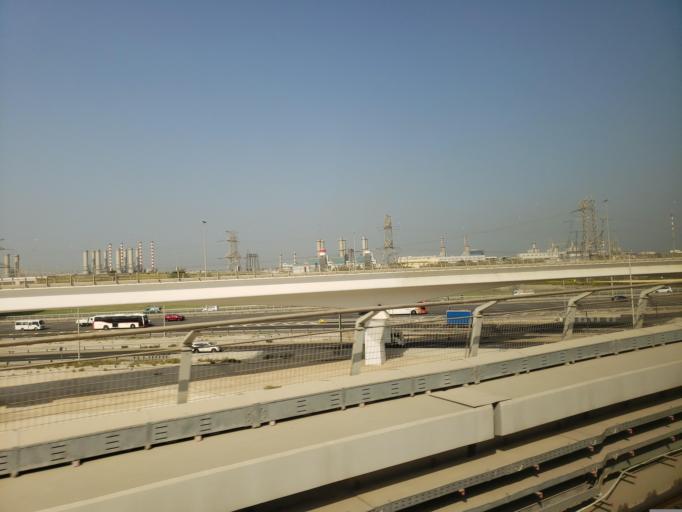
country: AE
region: Dubai
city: Dubai
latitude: 25.0536
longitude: 55.1256
